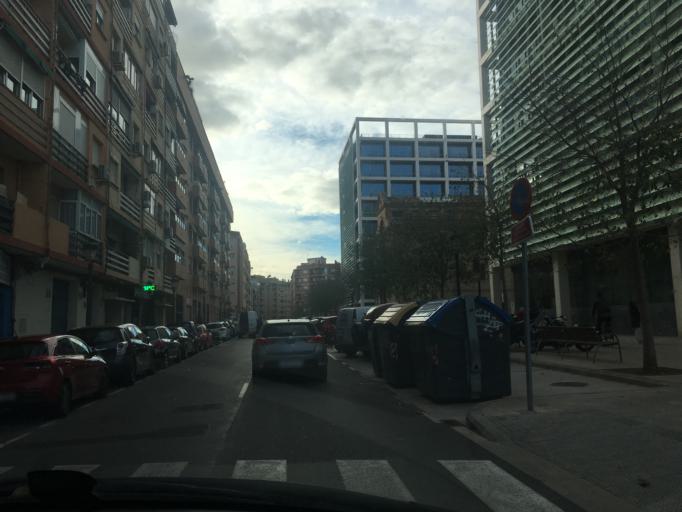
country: ES
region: Valencia
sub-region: Provincia de Valencia
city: Mislata
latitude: 39.4726
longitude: -0.4030
